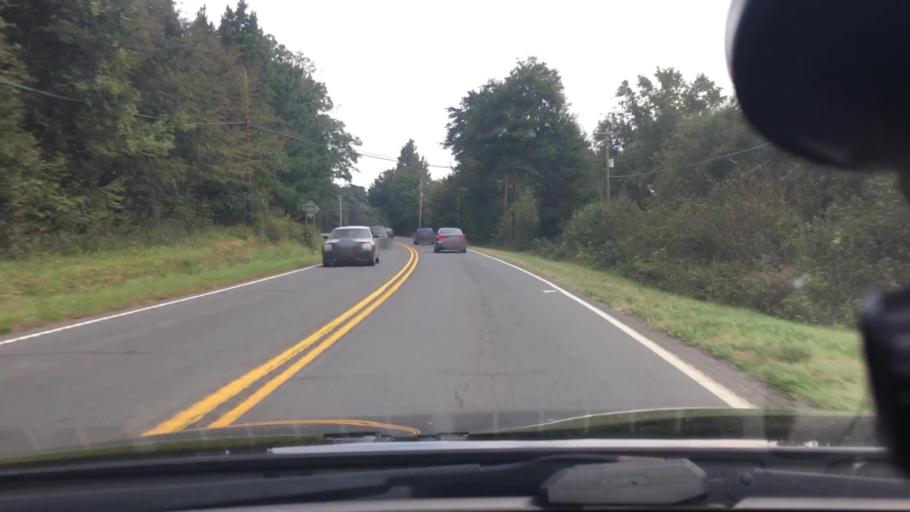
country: US
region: North Carolina
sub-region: Stanly County
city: Albemarle
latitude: 35.3289
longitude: -80.1335
